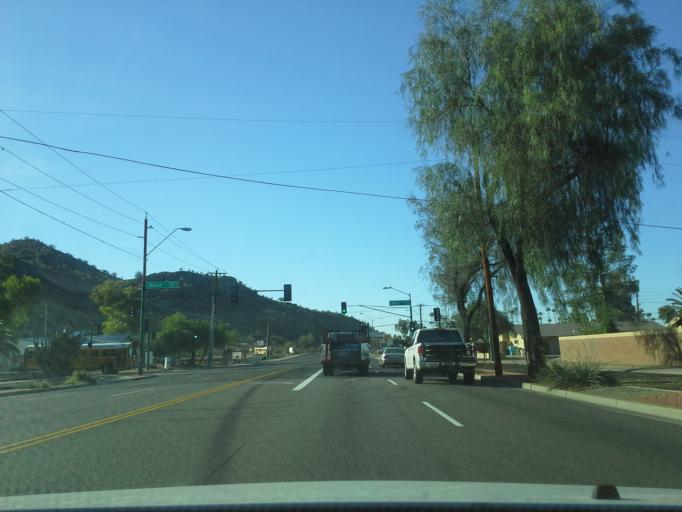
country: US
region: Arizona
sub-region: Maricopa County
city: Glendale
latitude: 33.6050
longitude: -112.0997
